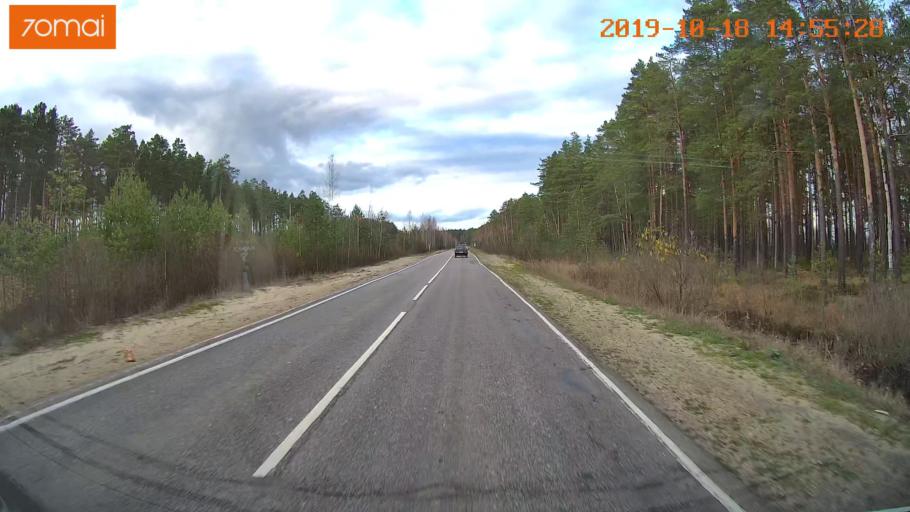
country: RU
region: Vladimir
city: Kurlovo
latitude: 55.4525
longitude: 40.5889
